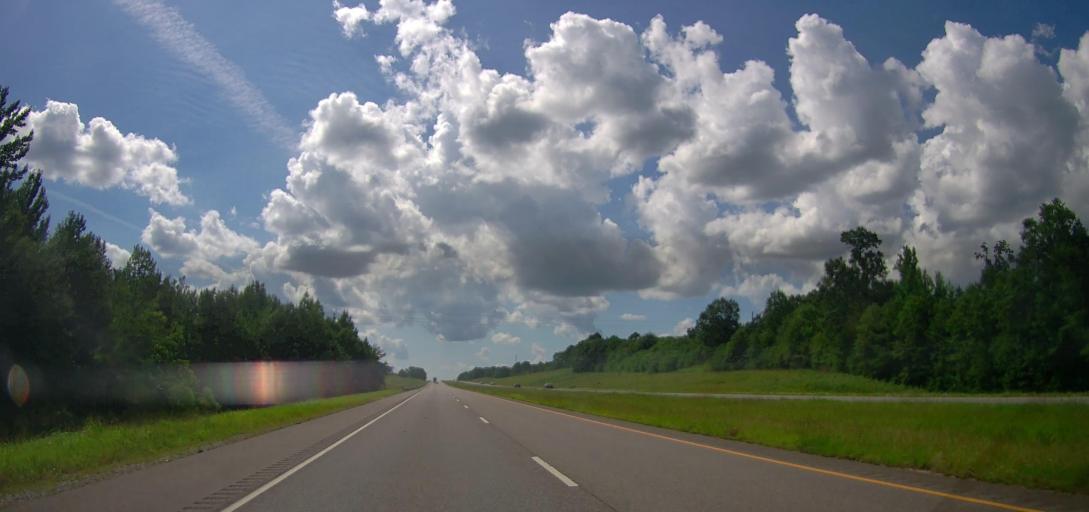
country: US
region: Alabama
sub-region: Pickens County
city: Reform
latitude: 33.3876
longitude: -88.0344
